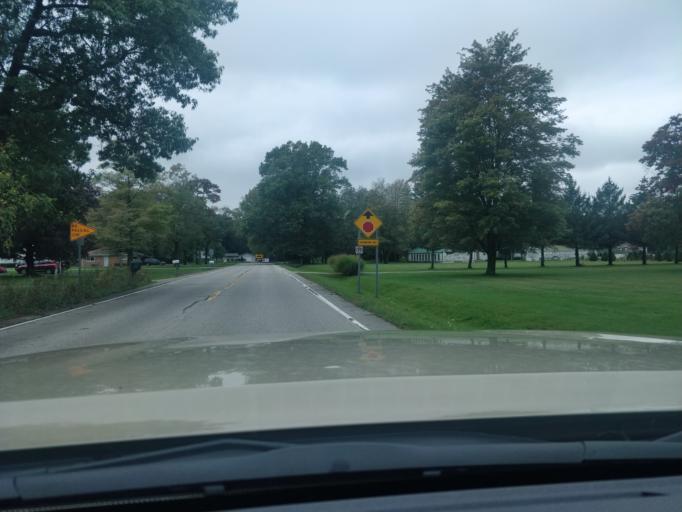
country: US
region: Michigan
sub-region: Wayne County
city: Romulus
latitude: 42.1795
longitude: -83.4141
